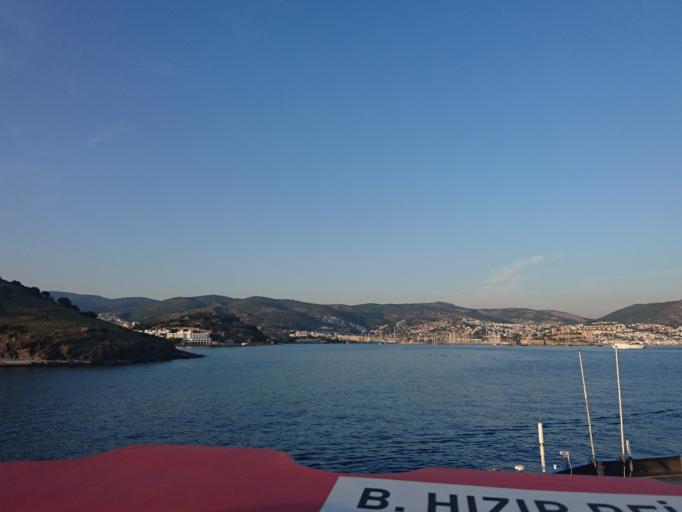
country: TR
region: Mugla
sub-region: Bodrum
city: Bodrum
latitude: 37.0198
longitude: 27.4194
